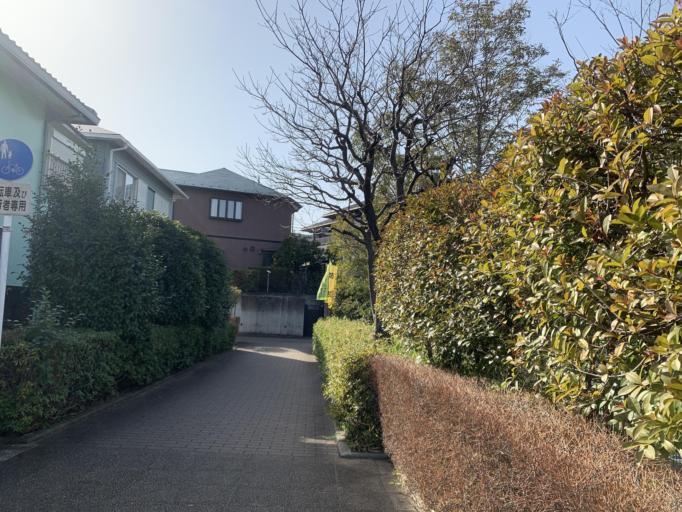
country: JP
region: Tokyo
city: Chofugaoka
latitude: 35.5513
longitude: 139.5844
